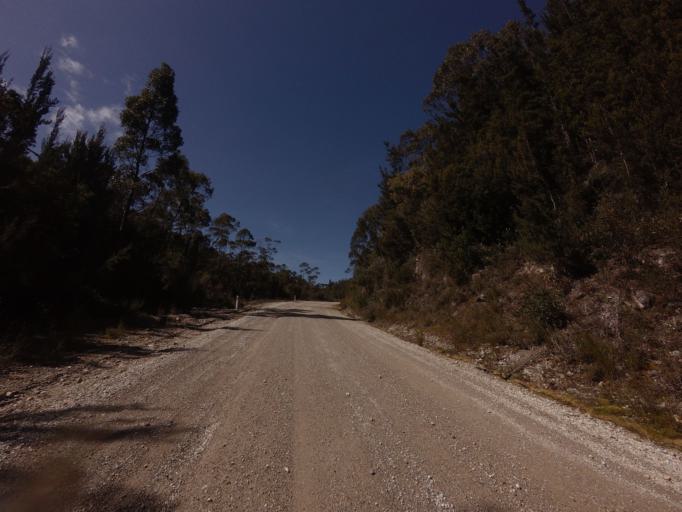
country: AU
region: Tasmania
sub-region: Huon Valley
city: Geeveston
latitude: -42.8175
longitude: 146.3870
